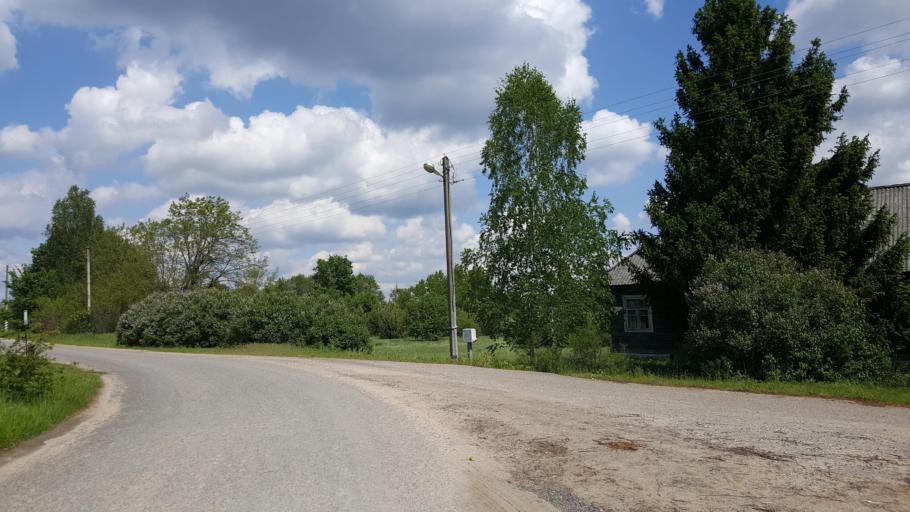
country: BY
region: Brest
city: Kamyanyets
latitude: 52.4429
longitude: 23.9793
